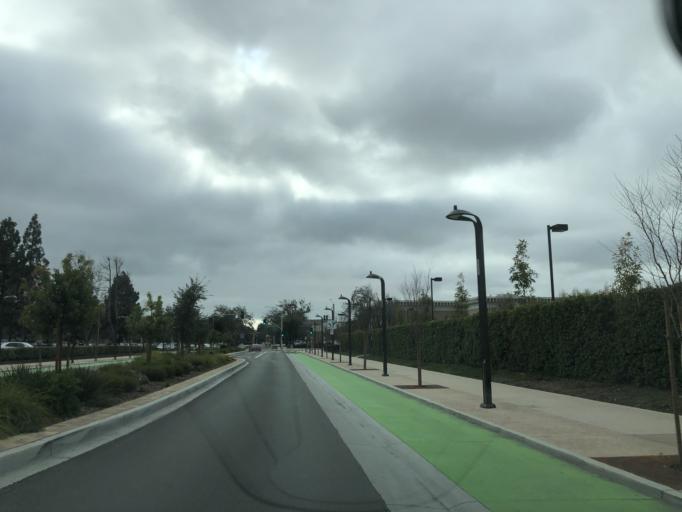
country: US
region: California
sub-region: Alameda County
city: Fremont
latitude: 37.5564
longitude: -121.9777
